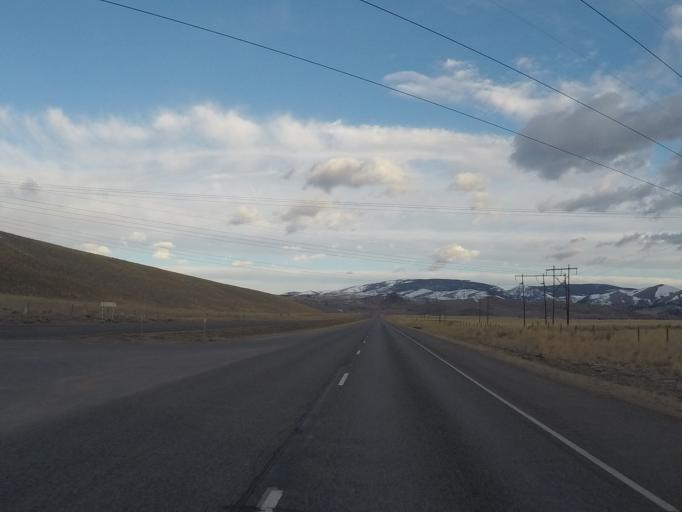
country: US
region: Montana
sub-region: Deer Lodge County
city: Anaconda
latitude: 46.1186
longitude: -112.8744
